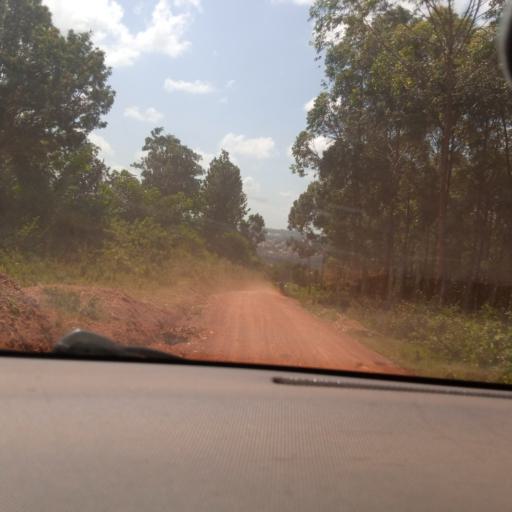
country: UG
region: Central Region
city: Masaka
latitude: -0.3231
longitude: 31.7430
